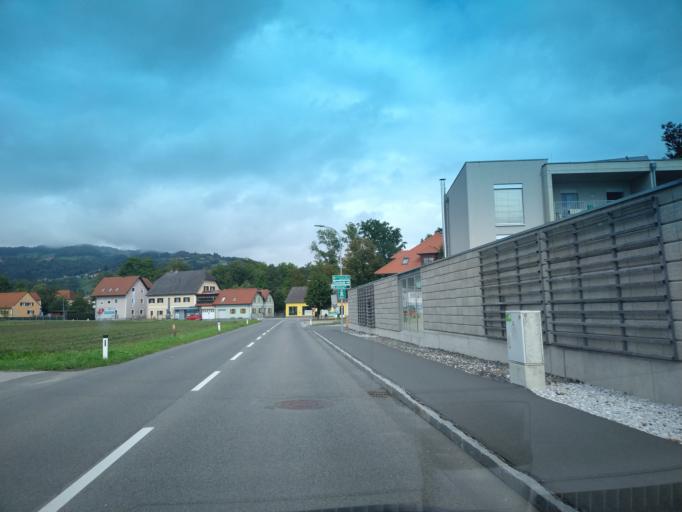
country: AT
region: Styria
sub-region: Politischer Bezirk Deutschlandsberg
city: Deutschlandsberg
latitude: 46.8147
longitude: 15.2222
